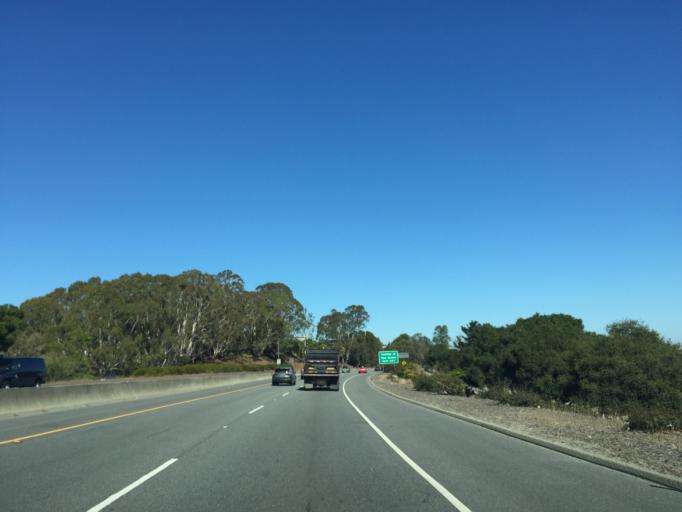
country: US
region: California
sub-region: San Mateo County
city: Highlands-Baywood Park
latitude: 37.5230
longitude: -122.3323
